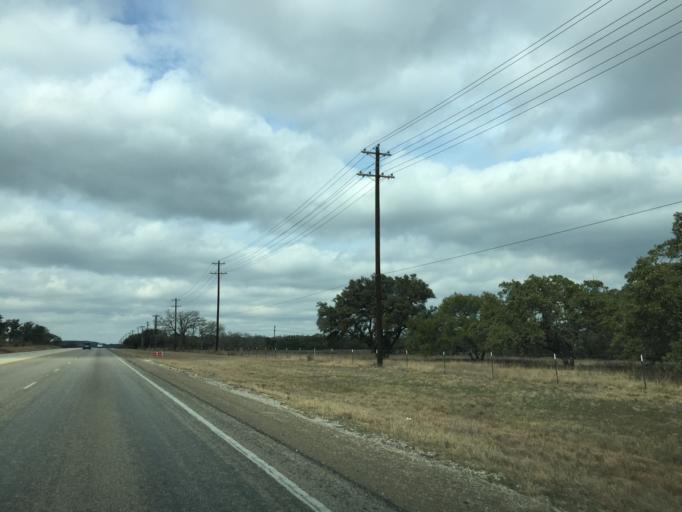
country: US
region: Texas
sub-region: Travis County
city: Briarcliff
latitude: 30.4135
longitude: -98.1154
